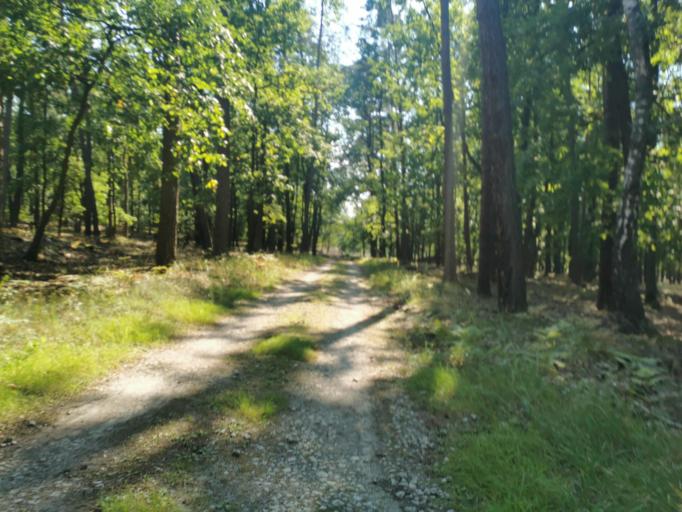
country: SK
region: Trnavsky
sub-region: Okres Senica
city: Senica
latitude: 48.6310
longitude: 17.2783
